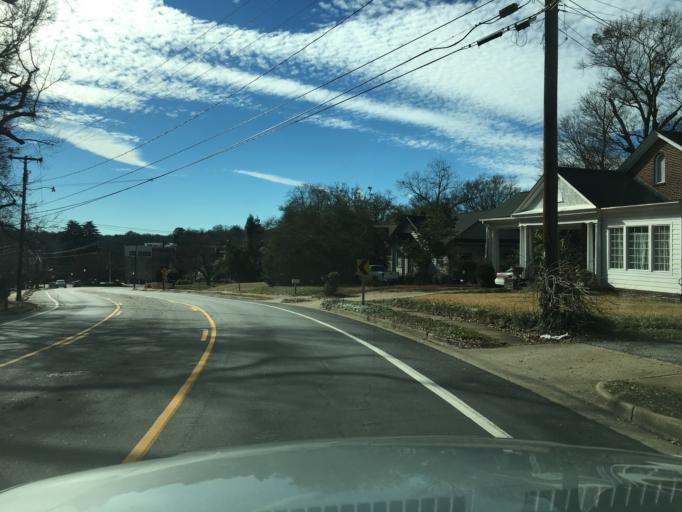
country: US
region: South Carolina
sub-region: Greenville County
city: Greenville
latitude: 34.8571
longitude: -82.3821
